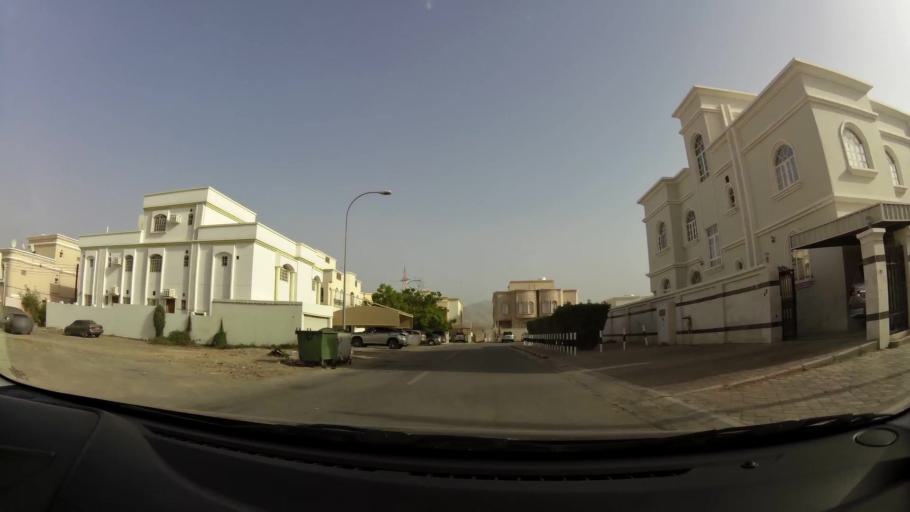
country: OM
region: Muhafazat Masqat
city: Bawshar
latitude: 23.5404
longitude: 58.3598
